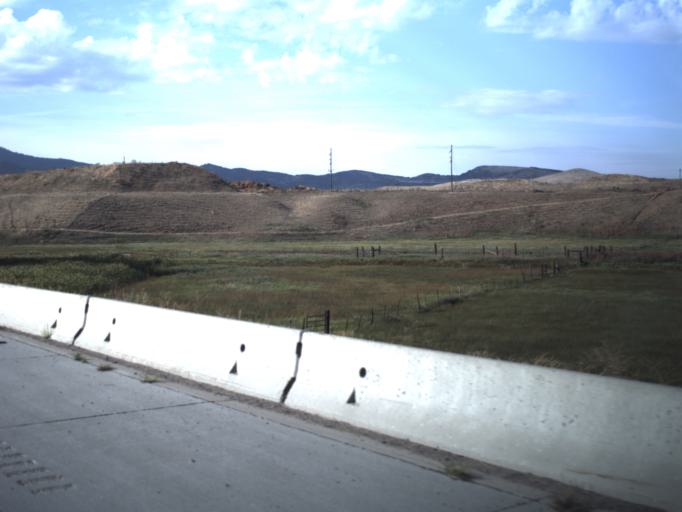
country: US
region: Utah
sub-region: Morgan County
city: Mountain Green
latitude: 41.1356
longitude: -111.7854
